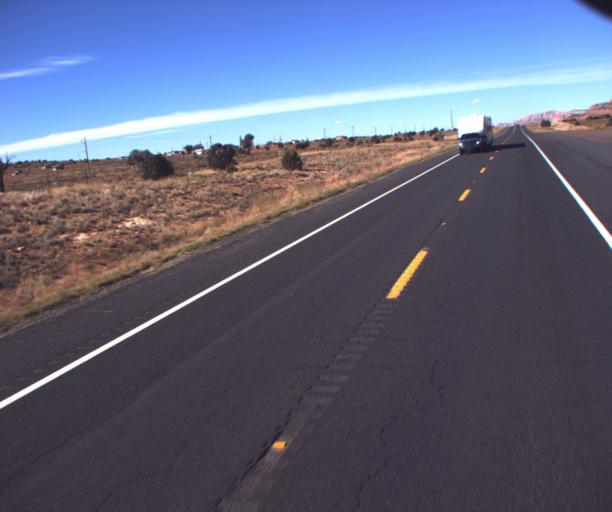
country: US
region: Arizona
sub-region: Coconino County
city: Tuba City
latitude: 36.3827
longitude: -111.5200
